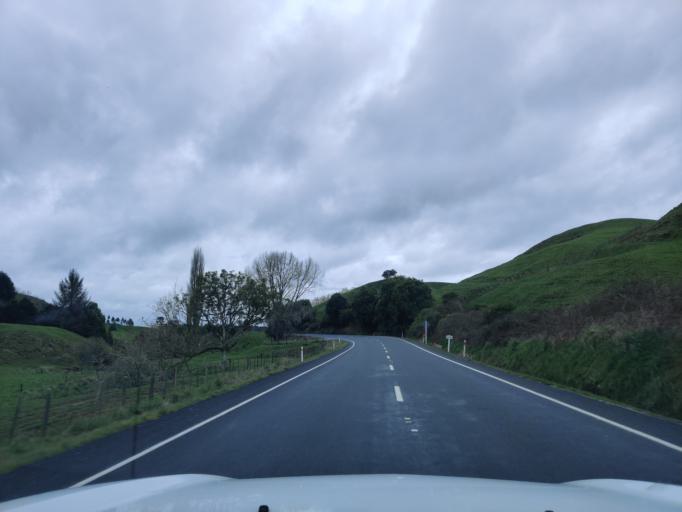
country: NZ
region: Waikato
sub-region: Otorohanga District
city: Otorohanga
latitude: -38.5378
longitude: 175.1784
